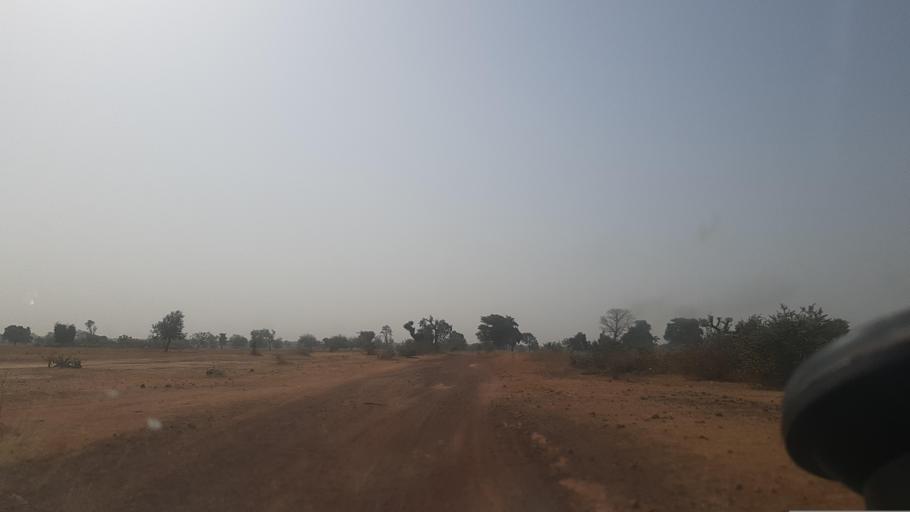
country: ML
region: Segou
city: Baroueli
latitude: 13.1526
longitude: -6.5163
